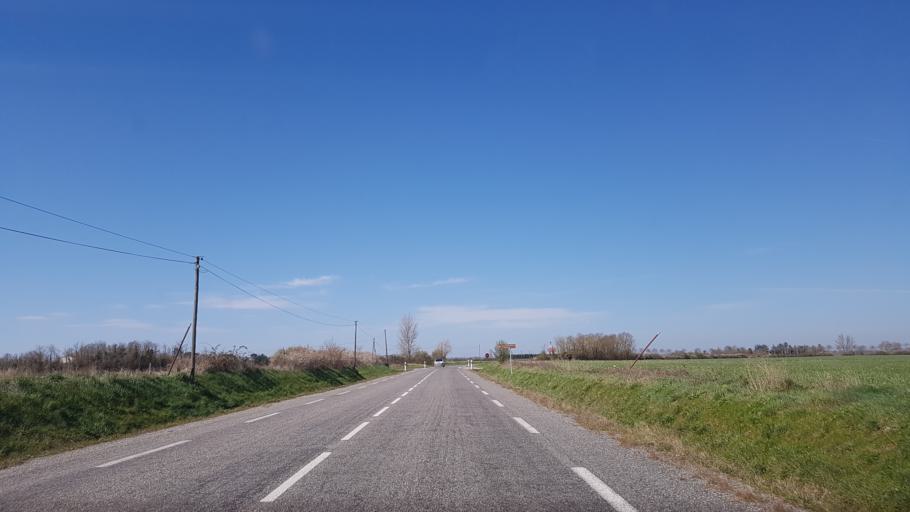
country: FR
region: Midi-Pyrenees
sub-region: Departement de l'Ariege
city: Mazeres
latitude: 43.2299
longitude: 1.6690
